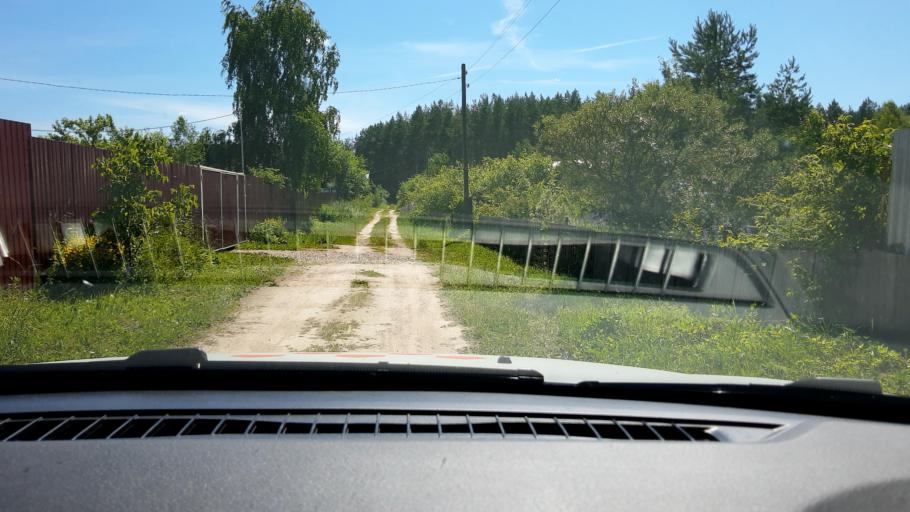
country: RU
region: Nizjnij Novgorod
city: Surovatikha
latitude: 55.8675
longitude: 43.9645
